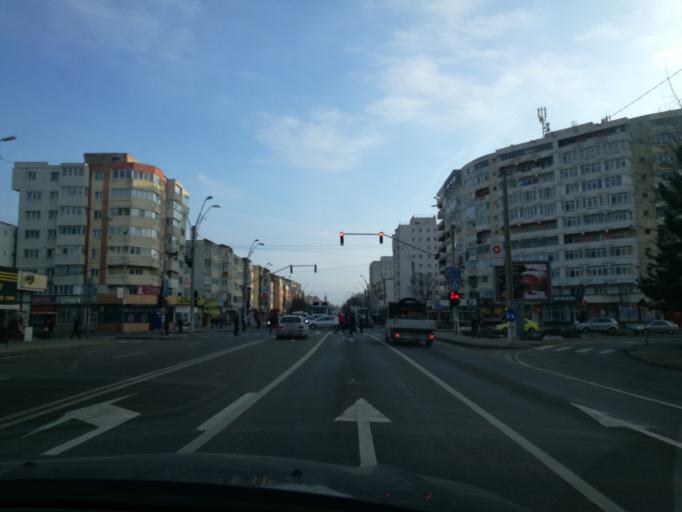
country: RO
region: Bacau
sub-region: Municipiul Bacau
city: Bacau
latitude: 46.5400
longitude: 26.9170
